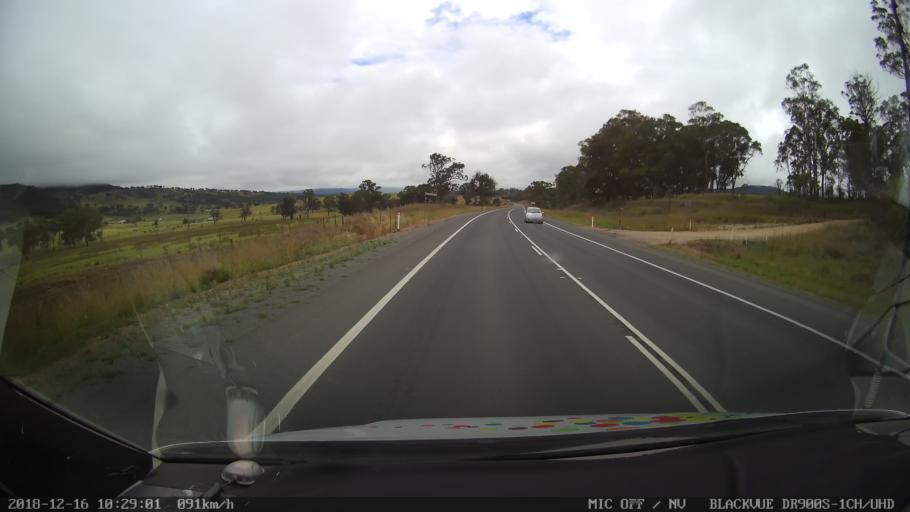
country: AU
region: New South Wales
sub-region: Tenterfield Municipality
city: Carrolls Creek
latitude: -29.1138
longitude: 151.9965
